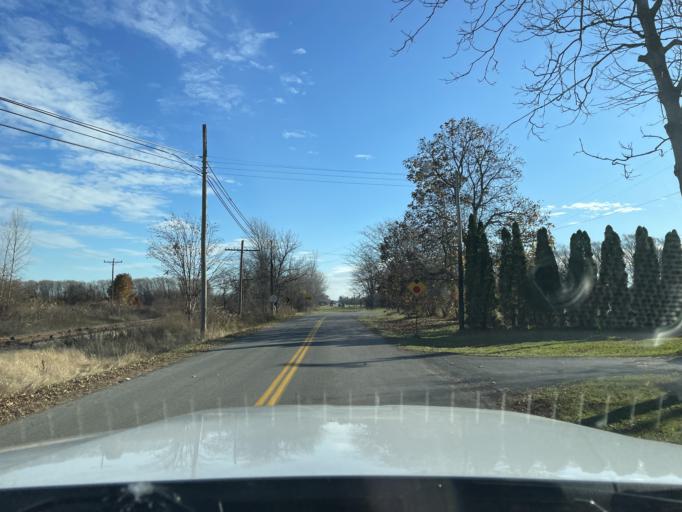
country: US
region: New York
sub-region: Niagara County
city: Middleport
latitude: 43.2061
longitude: -78.5181
